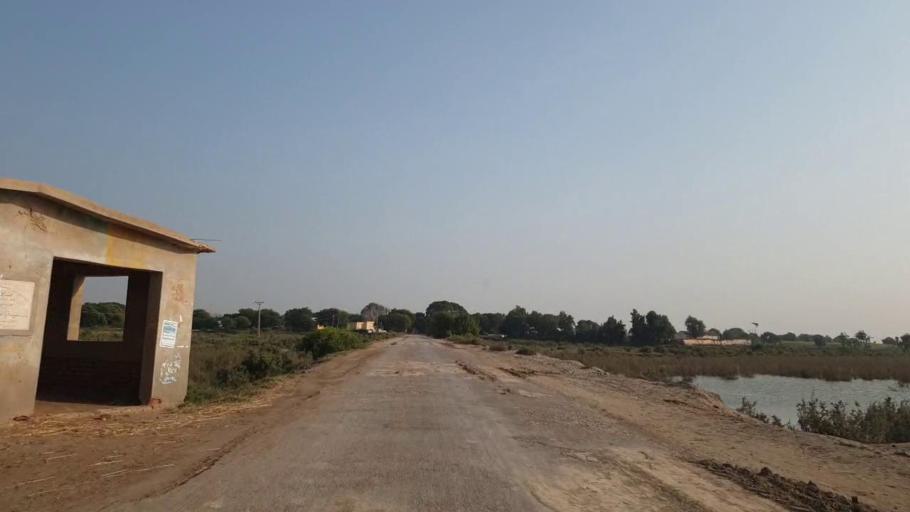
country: PK
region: Sindh
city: Bulri
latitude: 24.9882
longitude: 68.3901
